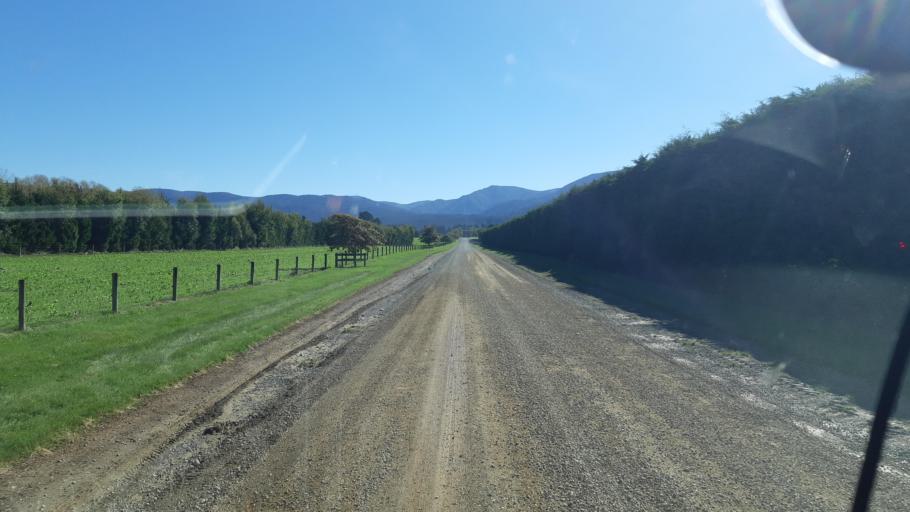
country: NZ
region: Canterbury
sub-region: Waimakariri District
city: Oxford
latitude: -43.2208
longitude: 172.3469
